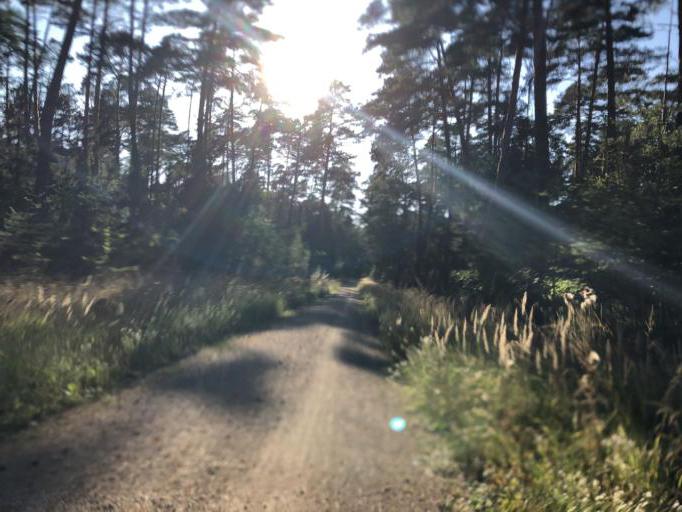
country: DE
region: Bavaria
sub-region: Regierungsbezirk Mittelfranken
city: Uttenreuth
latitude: 49.5589
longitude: 11.0857
